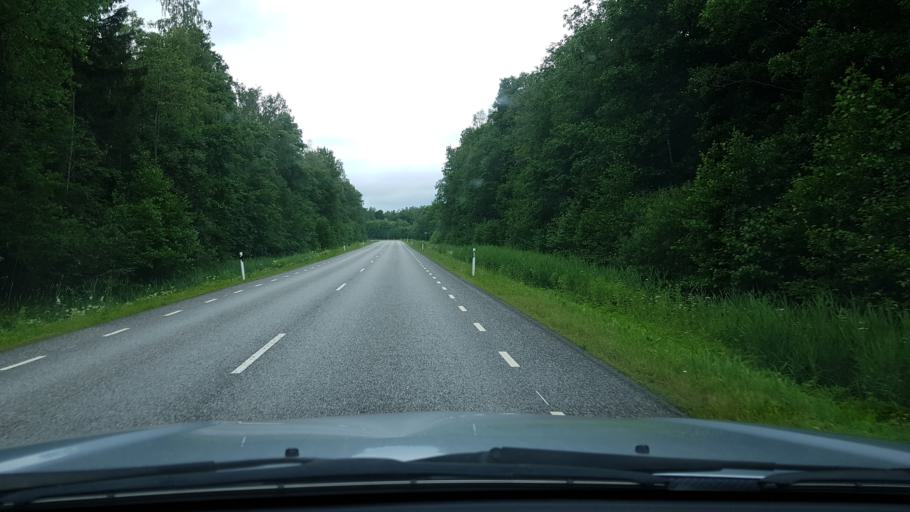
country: EE
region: Ida-Virumaa
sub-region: Narva-Joesuu linn
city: Narva-Joesuu
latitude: 59.3614
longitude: 27.9317
